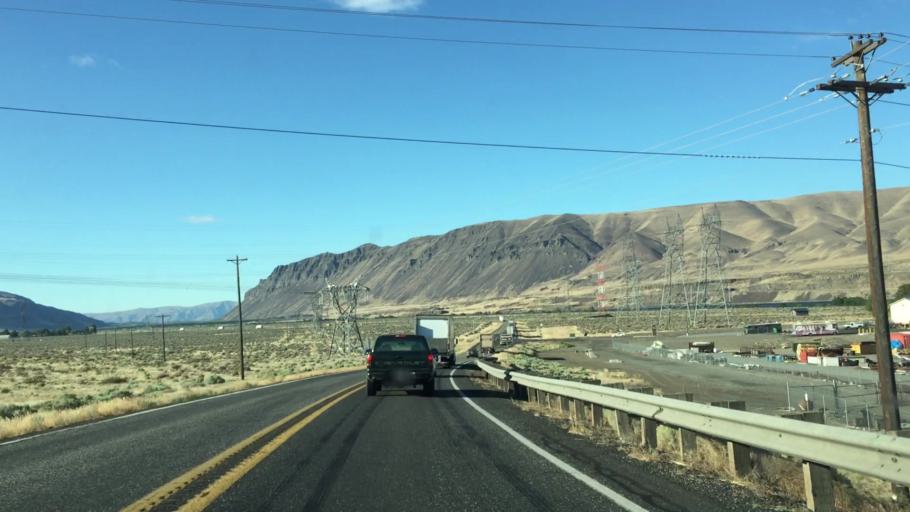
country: US
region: Washington
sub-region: Grant County
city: Mattawa
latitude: 46.8783
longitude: -119.9550
